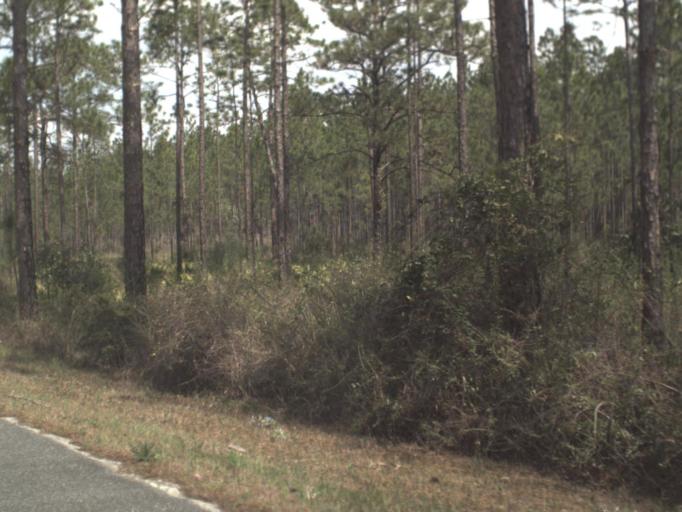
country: US
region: Florida
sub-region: Franklin County
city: Apalachicola
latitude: 29.9336
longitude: -84.9769
